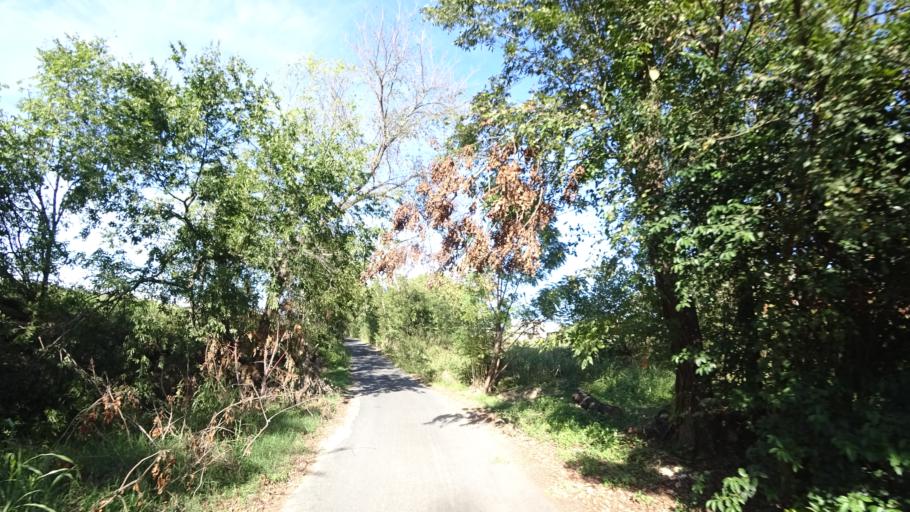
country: US
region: Texas
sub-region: Travis County
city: Austin
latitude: 30.2582
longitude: -97.6726
